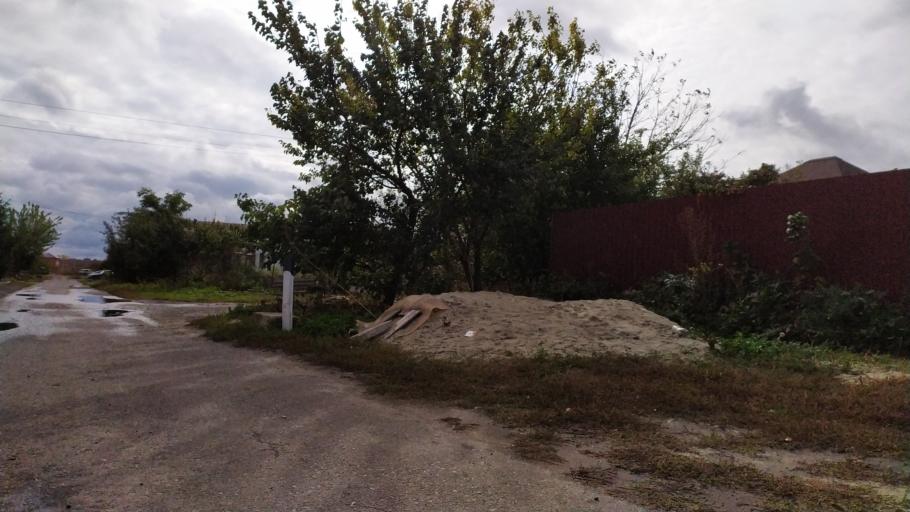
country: RU
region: Kursk
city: Kursk
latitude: 51.6433
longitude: 36.1548
